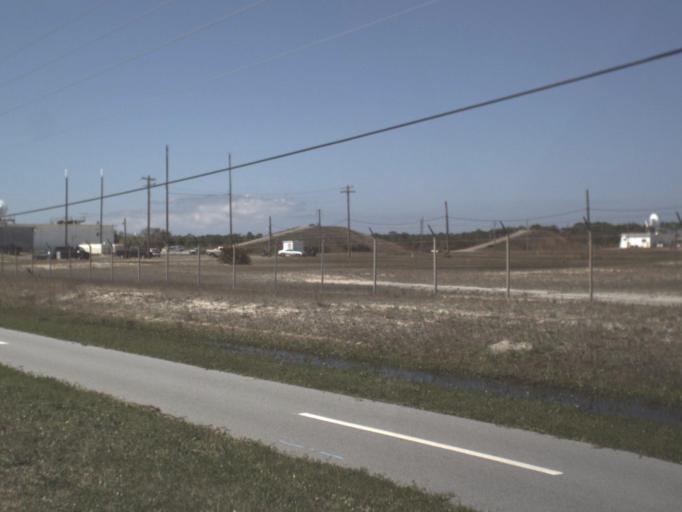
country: US
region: Florida
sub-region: Gulf County
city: Port Saint Joe
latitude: 29.6762
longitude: -85.3444
